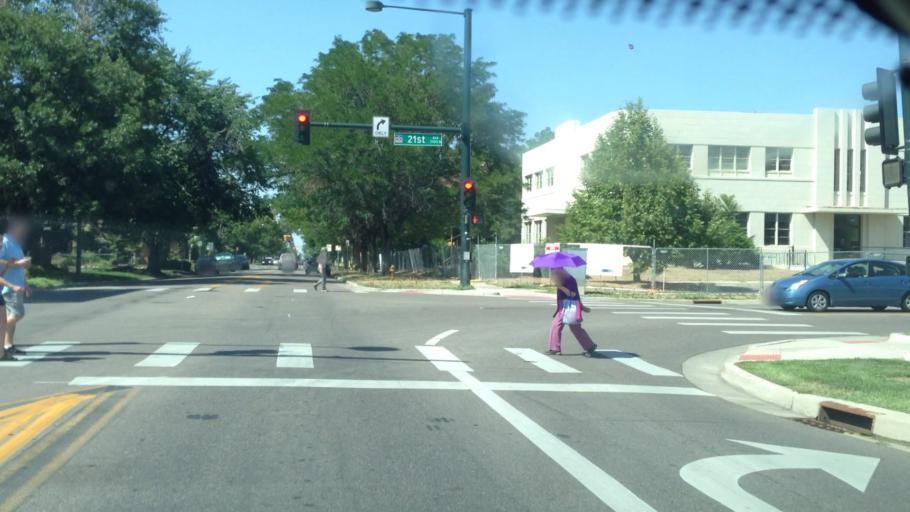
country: US
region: Colorado
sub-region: Denver County
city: Denver
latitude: 39.7479
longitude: -104.9733
